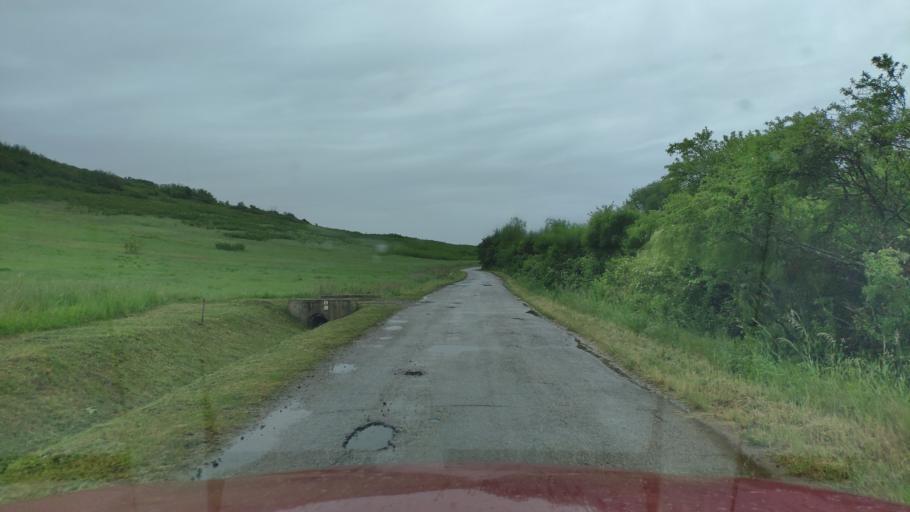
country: HU
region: Borsod-Abauj-Zemplen
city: Satoraljaujhely
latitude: 48.4294
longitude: 21.6967
